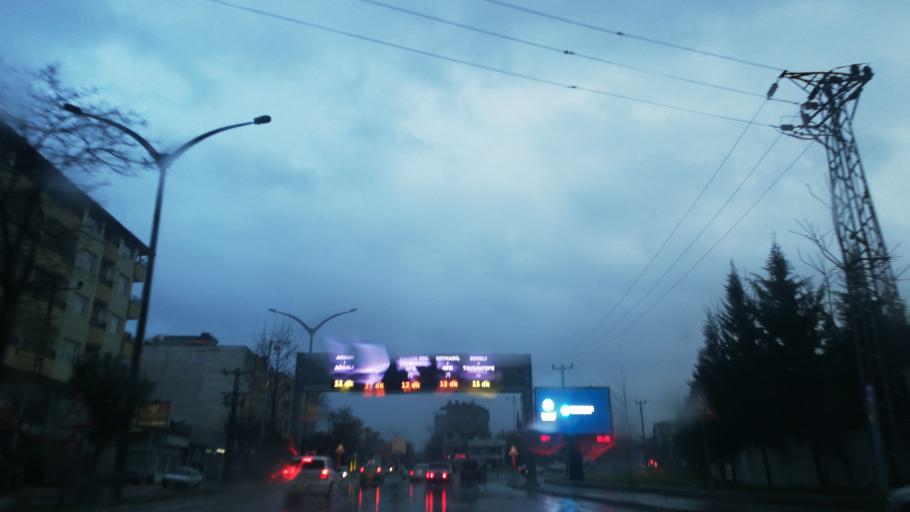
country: TR
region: Kahramanmaras
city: Kahramanmaras
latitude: 37.5657
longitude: 36.9503
